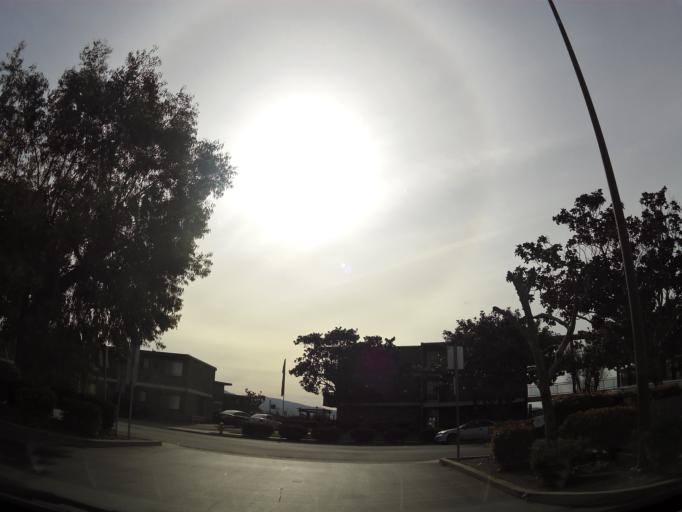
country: US
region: California
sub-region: Monterey County
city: Salinas
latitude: 36.6543
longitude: -121.6620
